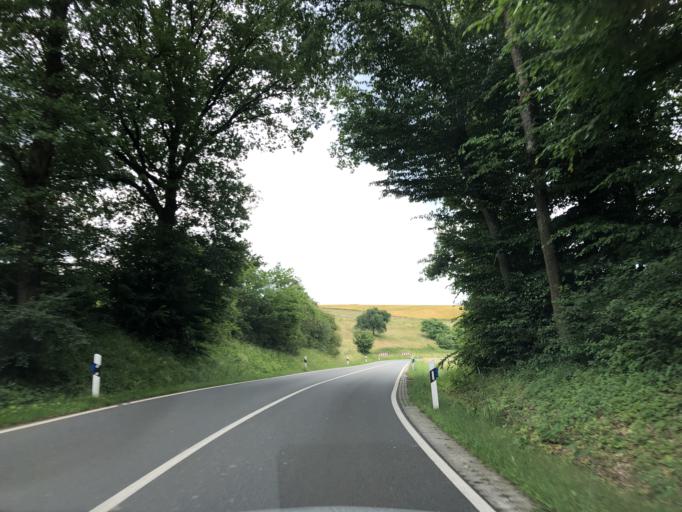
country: DE
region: Hesse
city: Michelstadt
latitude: 49.6961
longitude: 8.9788
